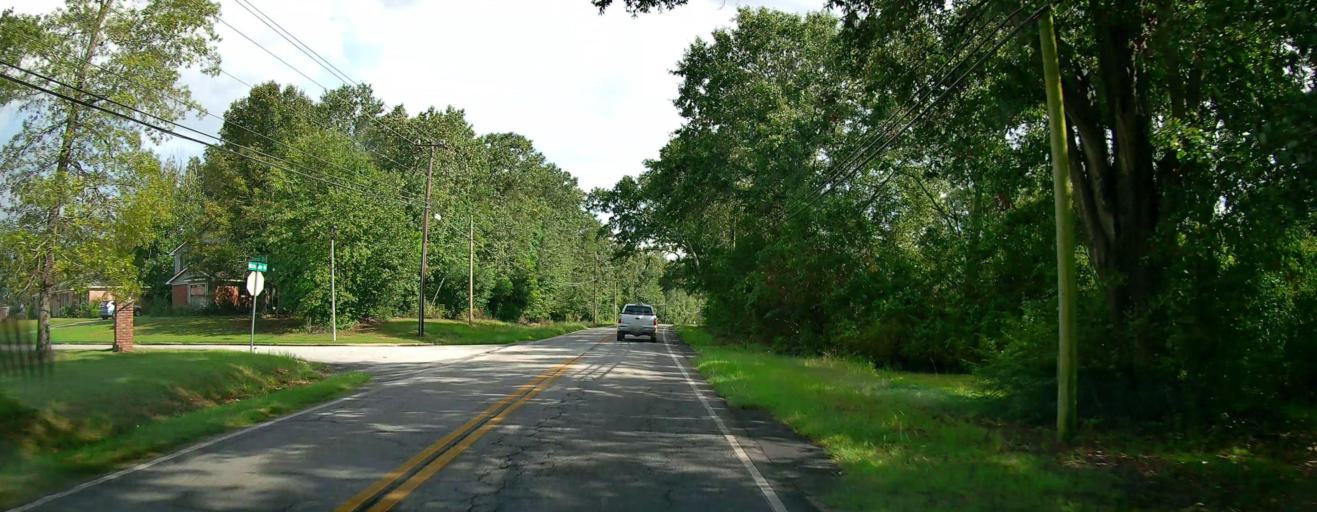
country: US
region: Alabama
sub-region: Russell County
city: Phenix City
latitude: 32.5479
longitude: -84.9691
